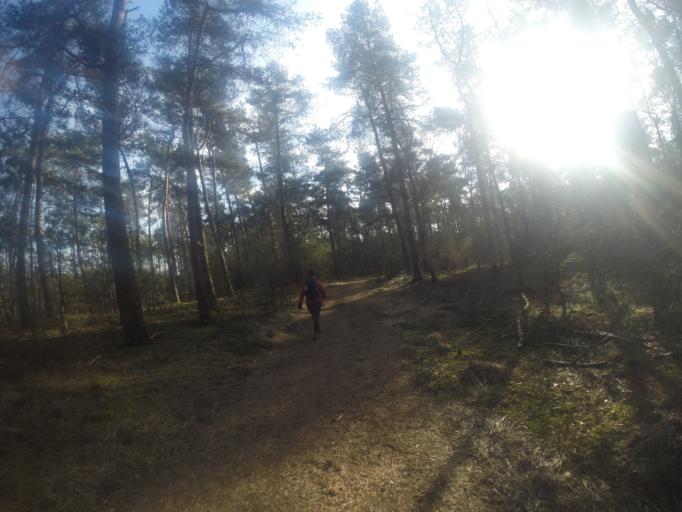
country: NL
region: Gelderland
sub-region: Gemeente Lochem
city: Almen
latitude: 52.1380
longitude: 6.3395
